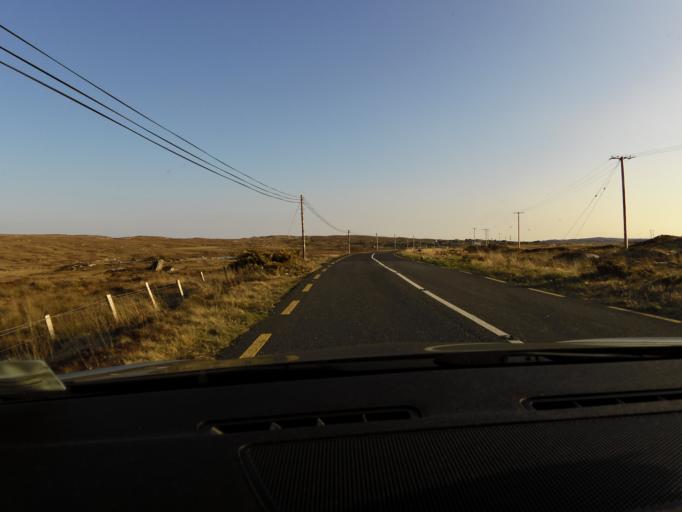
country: IE
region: Connaught
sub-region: County Galway
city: Oughterard
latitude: 53.3321
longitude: -9.5450
